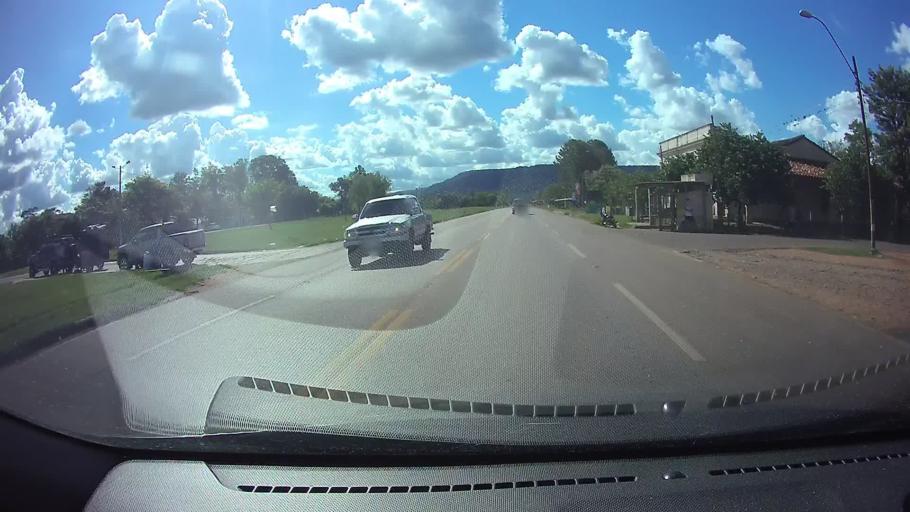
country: PY
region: Paraguari
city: Sapucai
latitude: -25.6913
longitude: -56.8626
